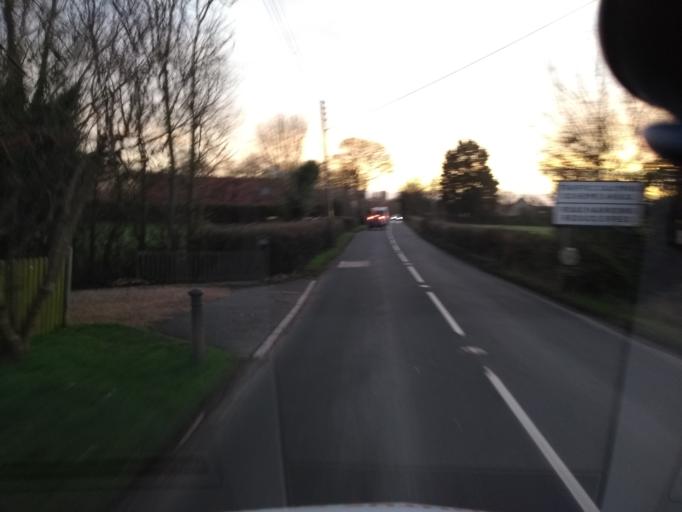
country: GB
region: England
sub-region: Somerset
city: Woolavington
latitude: 51.2257
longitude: -2.8972
